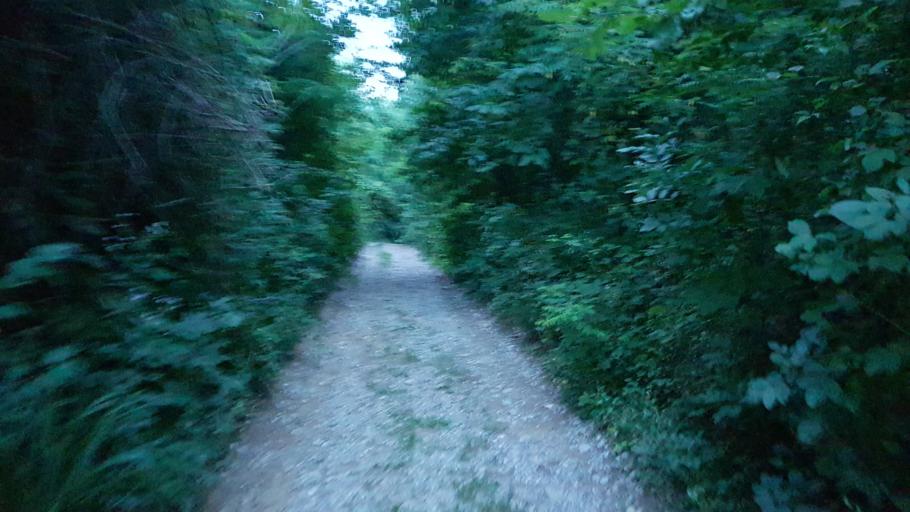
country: IT
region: Friuli Venezia Giulia
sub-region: Provincia di Gorizia
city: San Lorenzo Isontino
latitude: 45.9433
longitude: 13.5284
